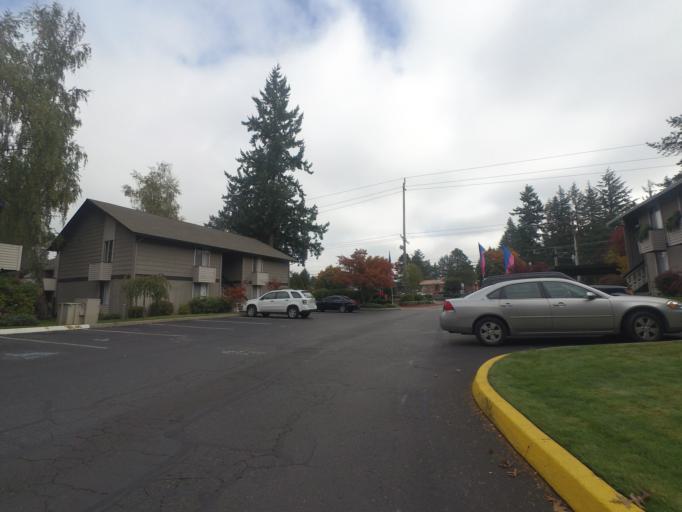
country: US
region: Washington
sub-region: Pierce County
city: Lakewood
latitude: 47.2029
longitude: -122.5093
